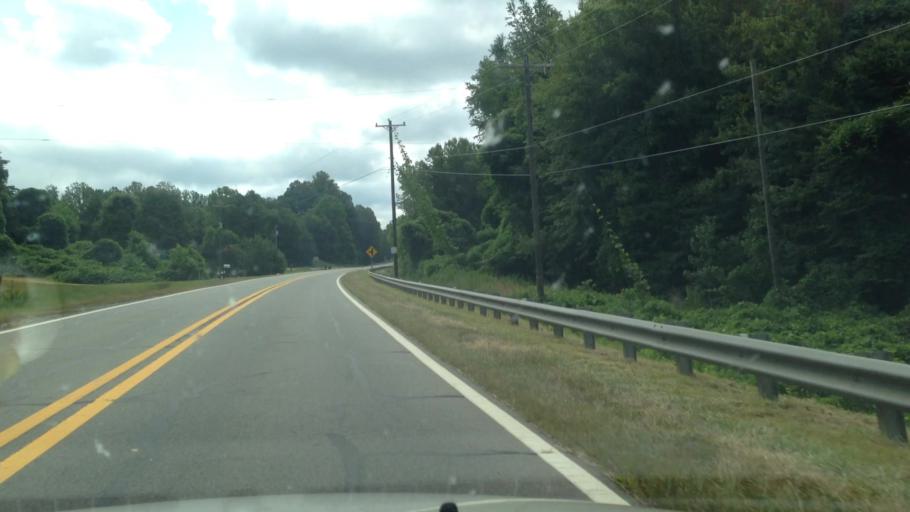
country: US
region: North Carolina
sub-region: Rockingham County
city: Wentworth
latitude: 36.3799
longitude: -79.8636
